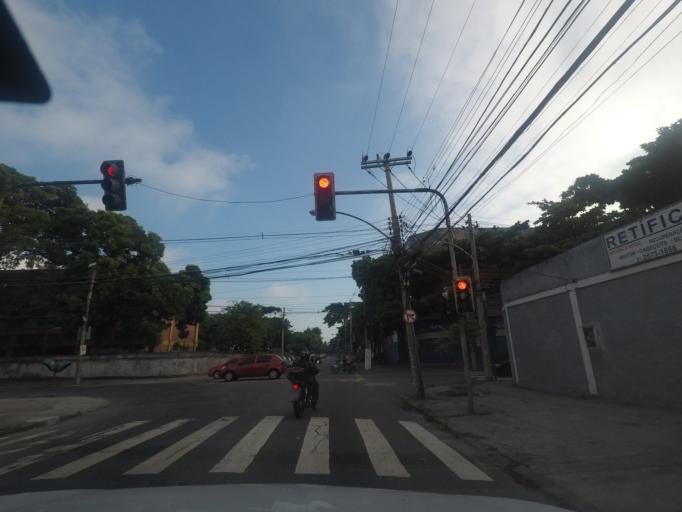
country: BR
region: Rio de Janeiro
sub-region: Duque De Caxias
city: Duque de Caxias
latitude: -22.8305
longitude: -43.2750
